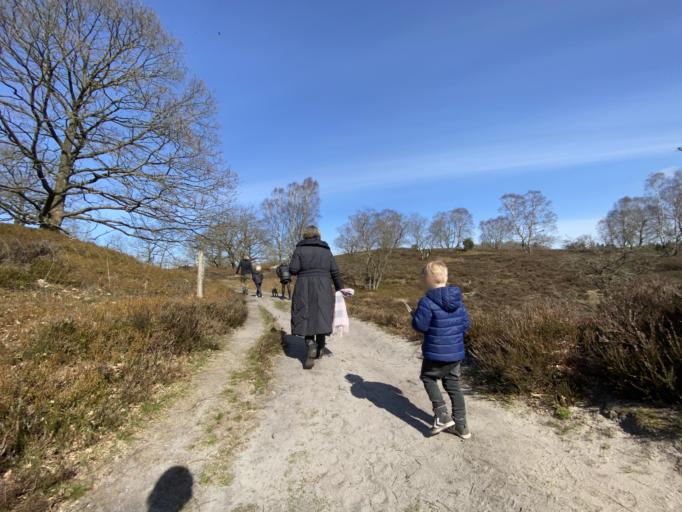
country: DK
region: Central Jutland
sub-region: Silkeborg Kommune
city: Svejbaek
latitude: 56.2164
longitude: 9.6944
